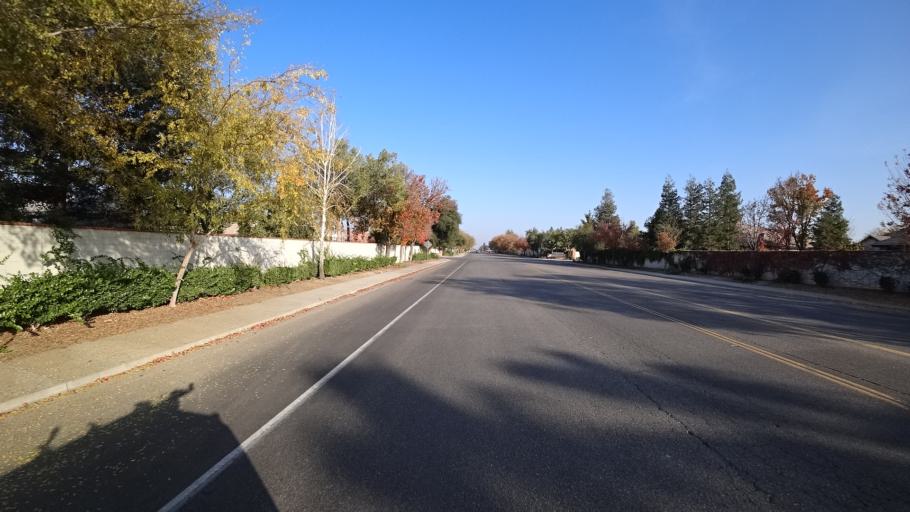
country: US
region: California
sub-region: Kern County
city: Rosedale
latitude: 35.3702
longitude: -119.1369
